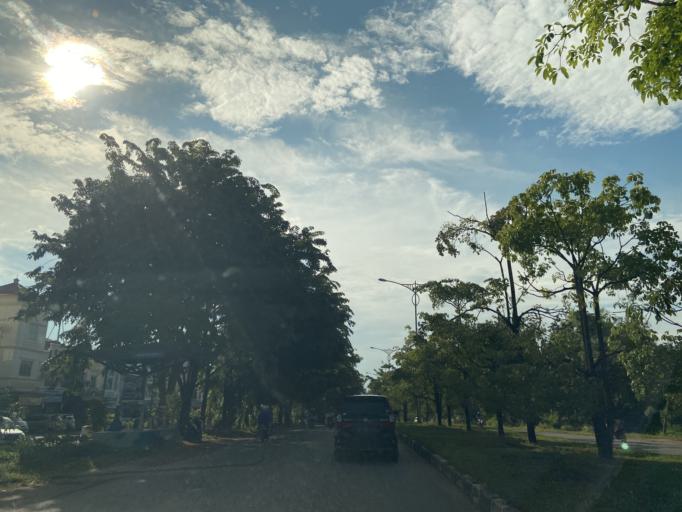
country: SG
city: Singapore
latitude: 1.1059
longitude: 104.0659
